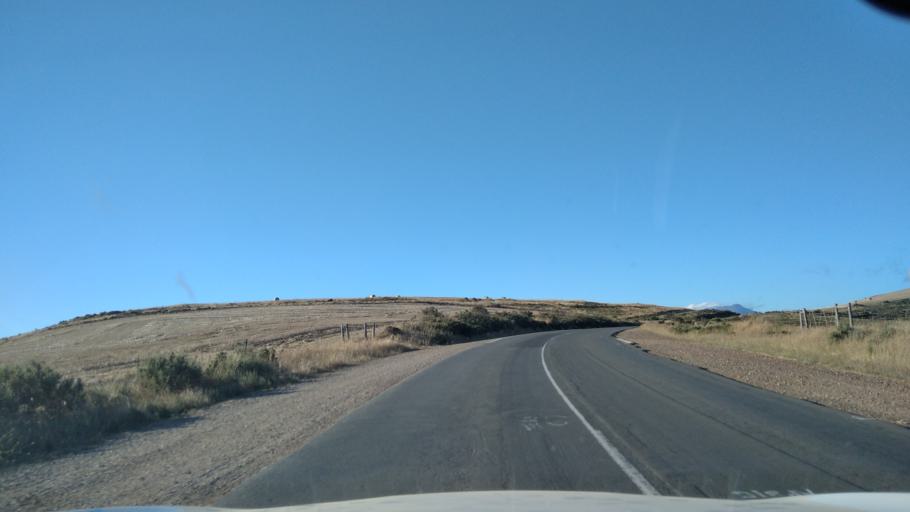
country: ZA
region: Western Cape
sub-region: Overberg District Municipality
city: Caledon
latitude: -34.1535
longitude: 19.3003
